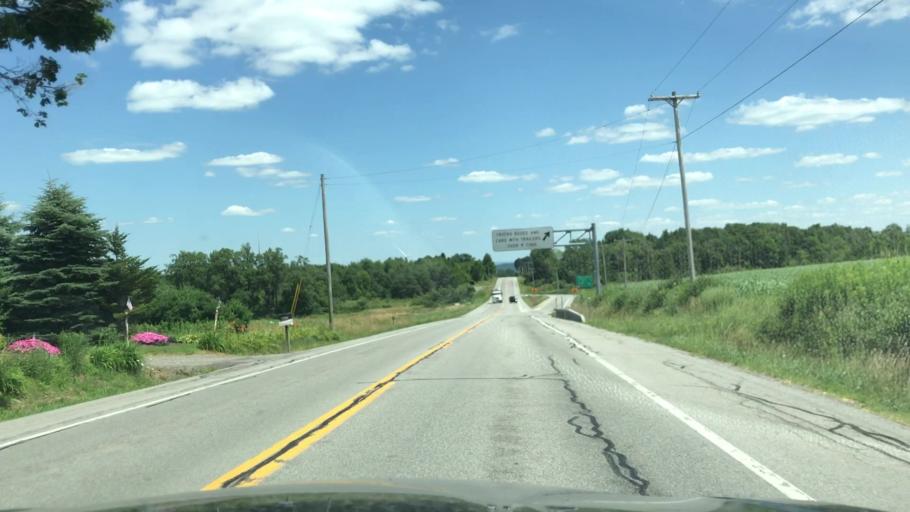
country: US
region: New York
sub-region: Wyoming County
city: Warsaw
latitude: 42.7469
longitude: -78.2280
